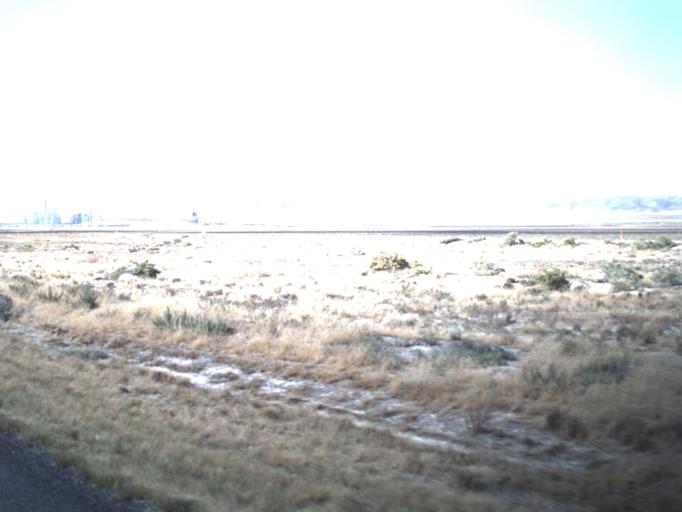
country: US
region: Utah
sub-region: Millard County
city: Delta
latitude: 38.9554
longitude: -112.8052
